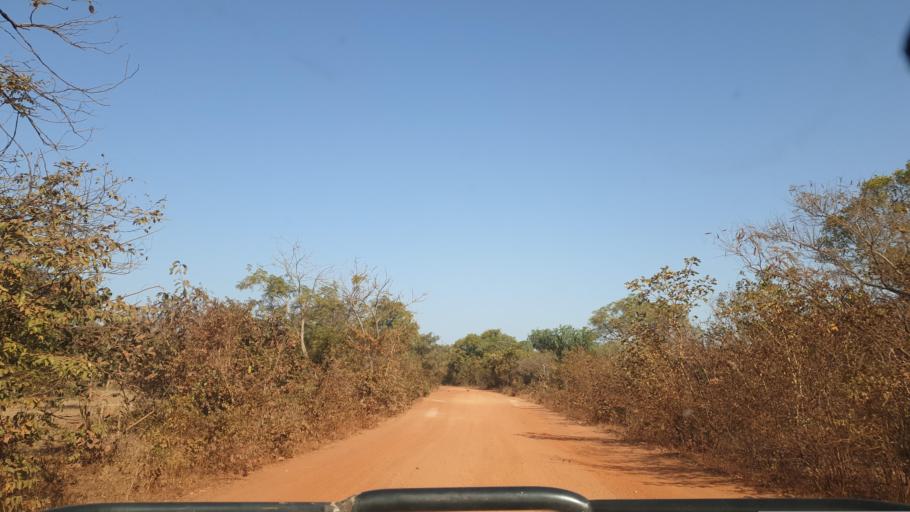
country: ML
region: Sikasso
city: Bougouni
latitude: 11.7825
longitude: -6.9084
